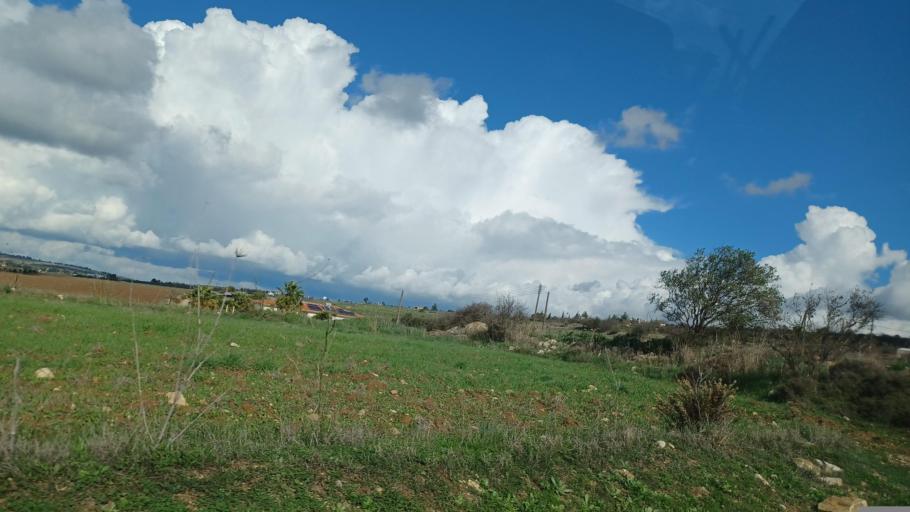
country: CY
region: Pafos
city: Pegeia
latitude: 34.9138
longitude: 32.4174
